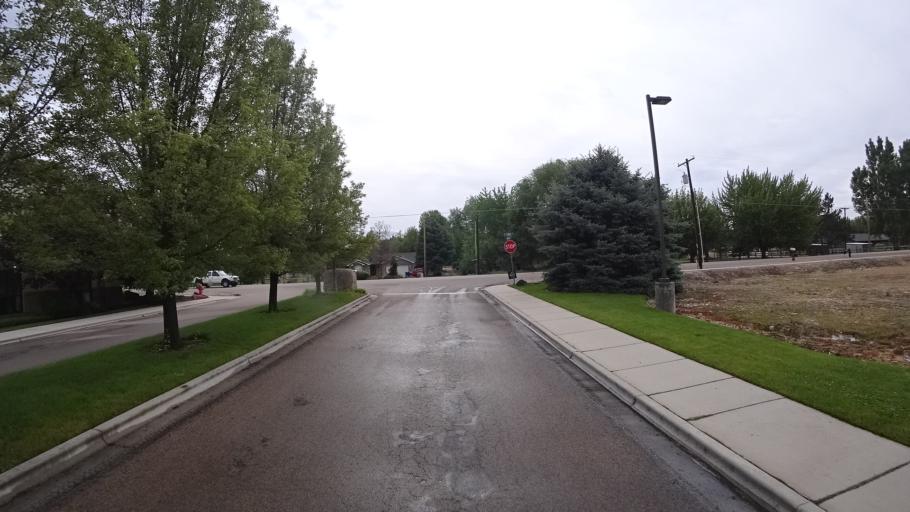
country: US
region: Idaho
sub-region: Ada County
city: Star
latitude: 43.6855
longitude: -116.4936
